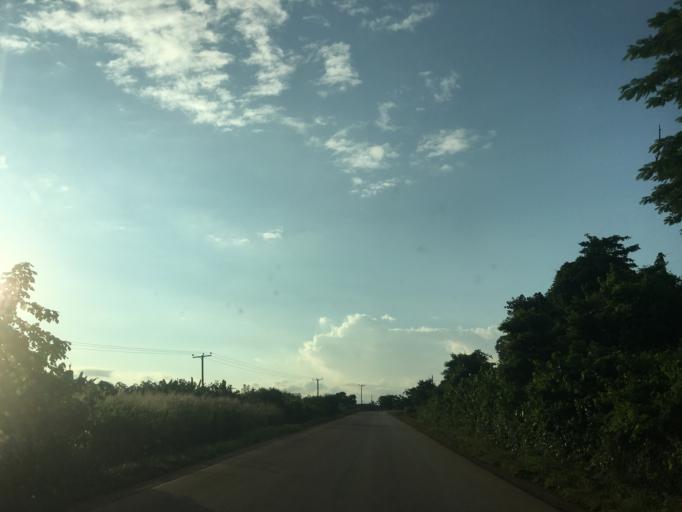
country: GH
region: Western
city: Bibiani
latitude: 6.5657
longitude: -2.3706
